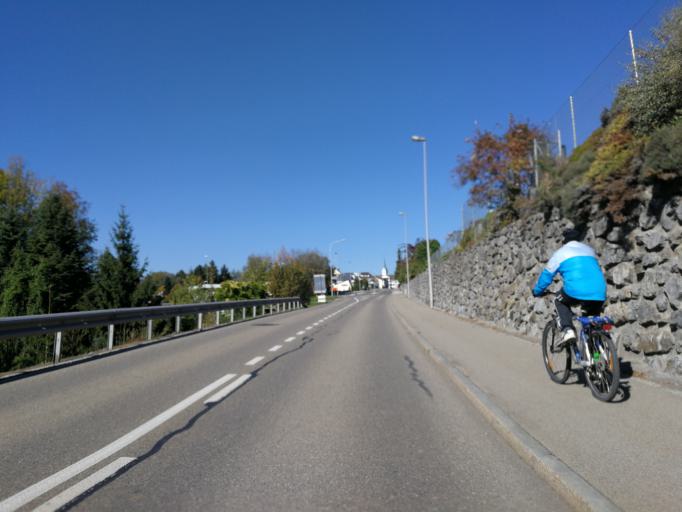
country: CH
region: Zurich
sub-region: Bezirk Meilen
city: Hombrechtikon
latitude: 47.2479
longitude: 8.7699
